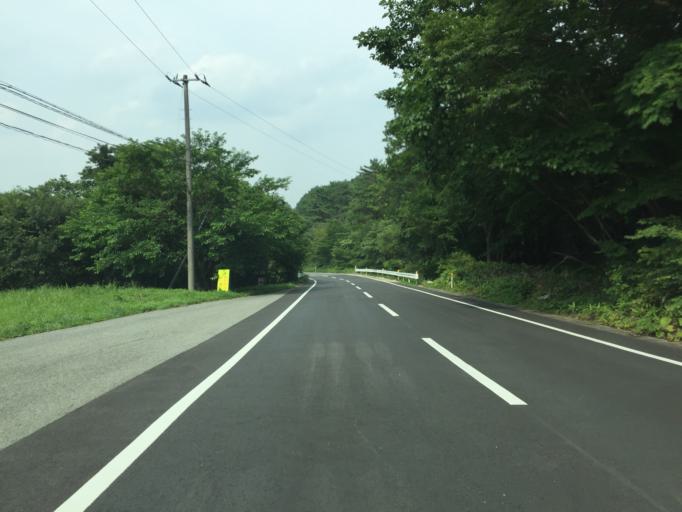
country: JP
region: Fukushima
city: Funehikimachi-funehiki
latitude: 37.4849
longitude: 140.7633
